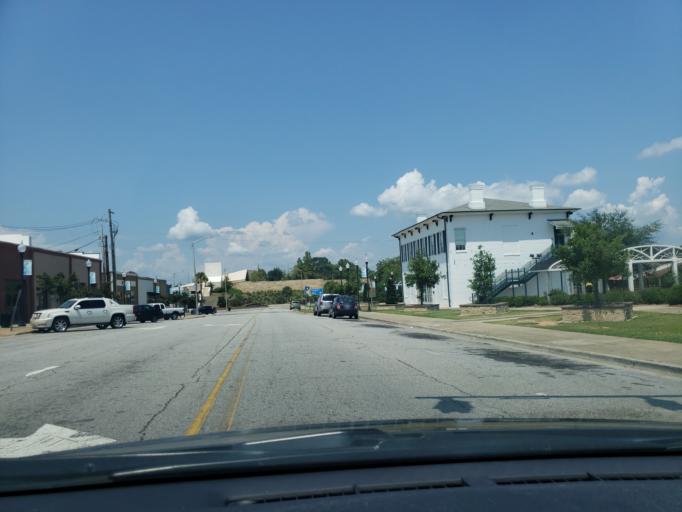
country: US
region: Georgia
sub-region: Dougherty County
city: Albany
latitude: 31.5770
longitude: -84.1490
